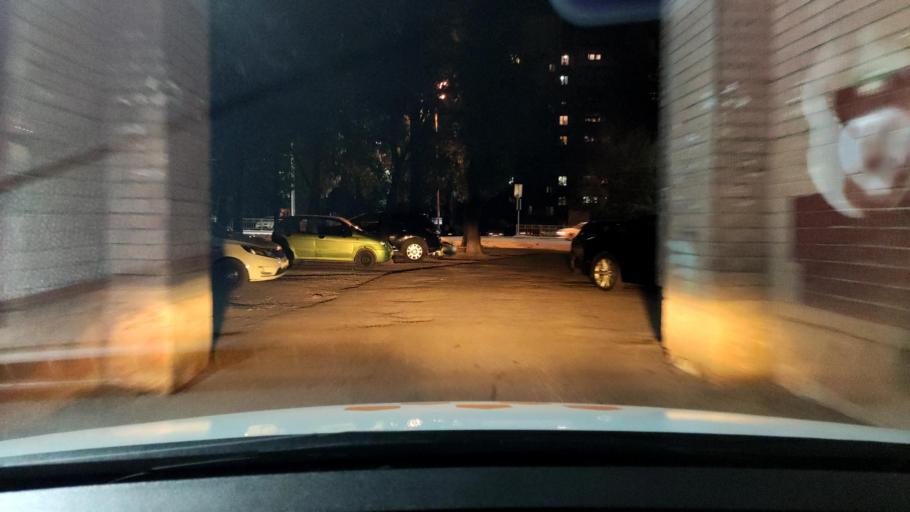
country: RU
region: Voronezj
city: Podgornoye
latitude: 51.7015
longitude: 39.1447
